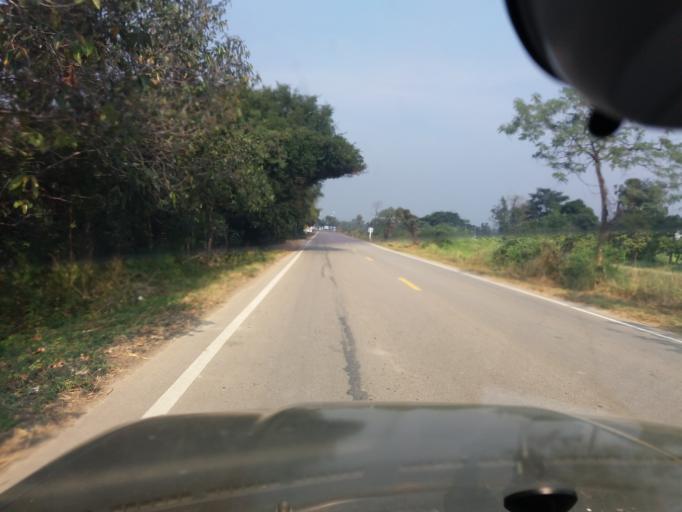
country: TH
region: Sing Buri
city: Bang Racham
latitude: 14.9142
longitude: 100.2561
